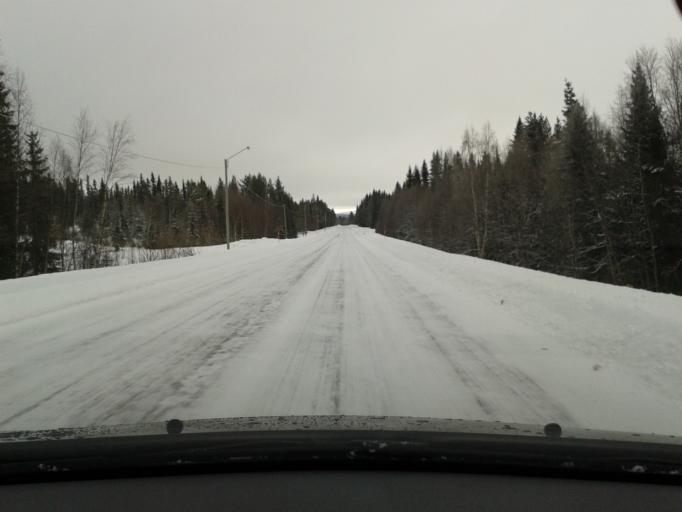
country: SE
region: Vaesterbotten
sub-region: Vilhelmina Kommun
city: Sjoberg
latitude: 64.8418
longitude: 15.9182
